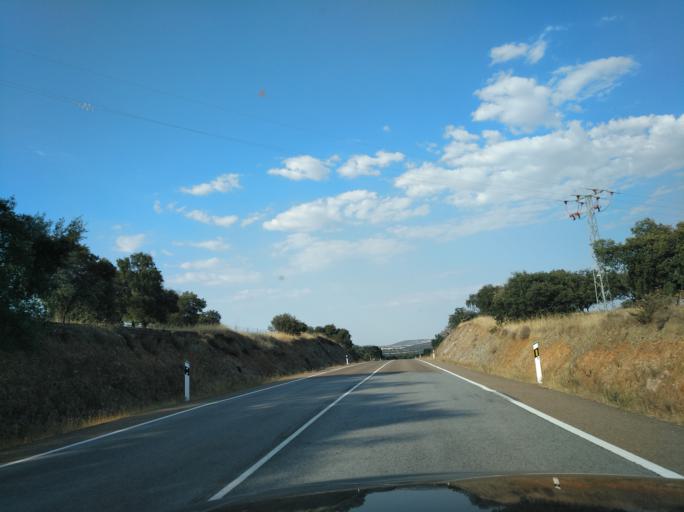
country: ES
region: Extremadura
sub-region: Provincia de Badajoz
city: Alconchel
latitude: 38.4487
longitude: -7.0867
